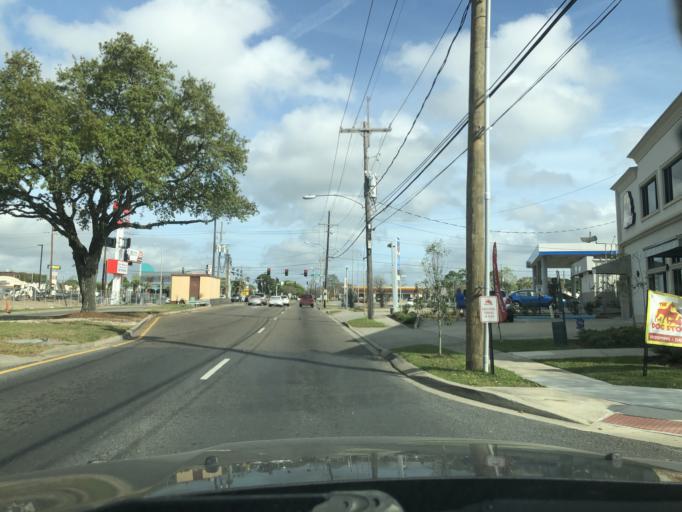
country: US
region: Louisiana
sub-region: Jefferson Parish
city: Metairie Terrace
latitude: 30.0046
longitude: -90.1946
